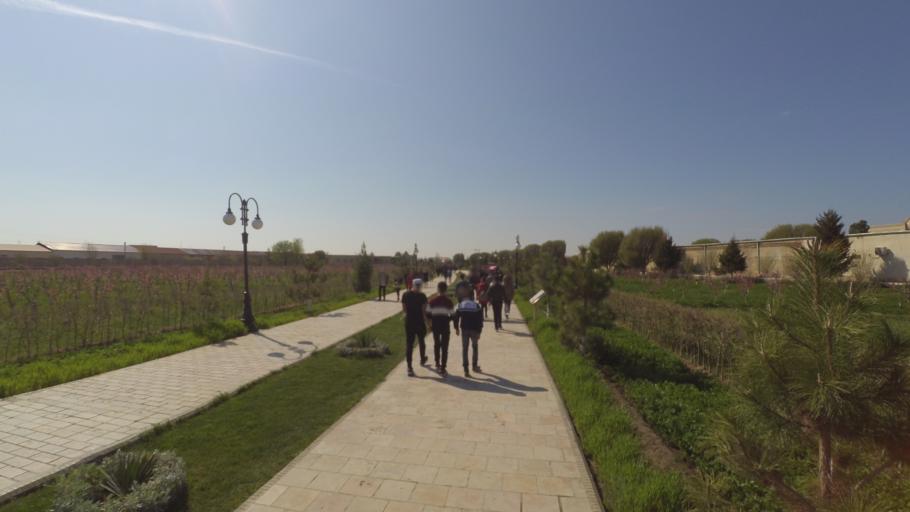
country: UZ
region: Bukhara
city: Kogon
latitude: 39.8026
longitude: 64.5387
